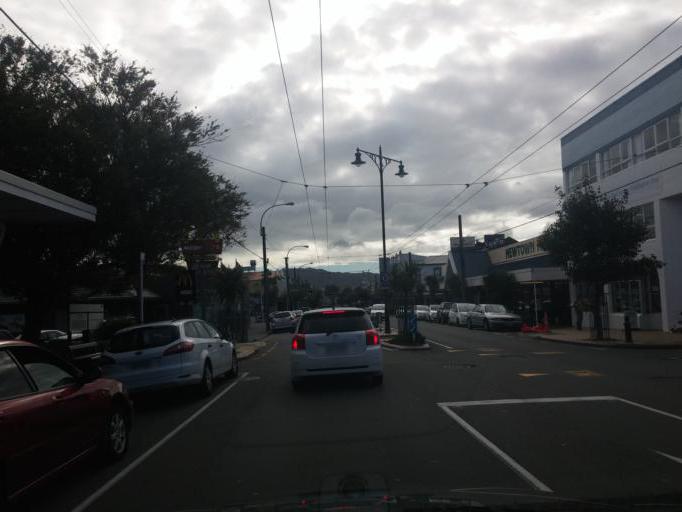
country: NZ
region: Wellington
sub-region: Wellington City
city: Wellington
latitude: -41.3150
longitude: 174.7802
